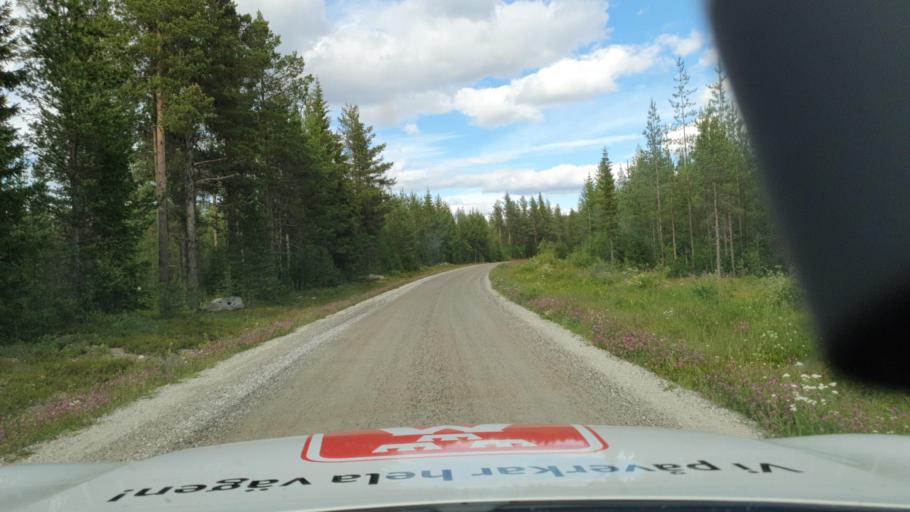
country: SE
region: Vaesterbotten
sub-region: Asele Kommun
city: Insjon
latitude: 64.2037
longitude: 17.7955
